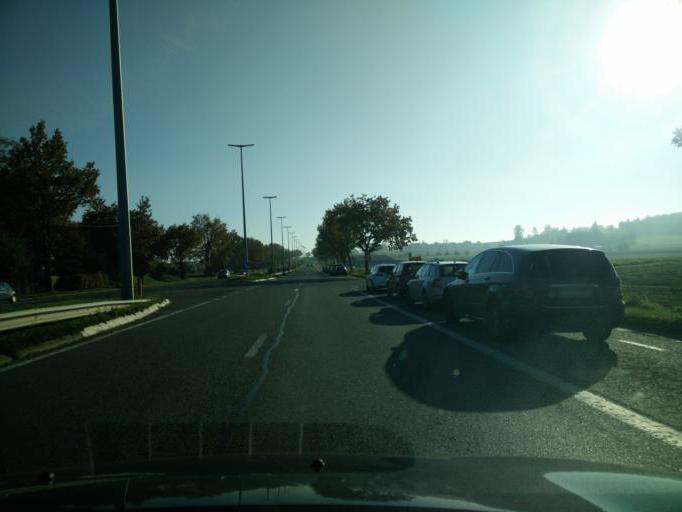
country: BE
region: Flanders
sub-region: Provincie Oost-Vlaanderen
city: Oudenaarde
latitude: 50.8230
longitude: 3.6037
